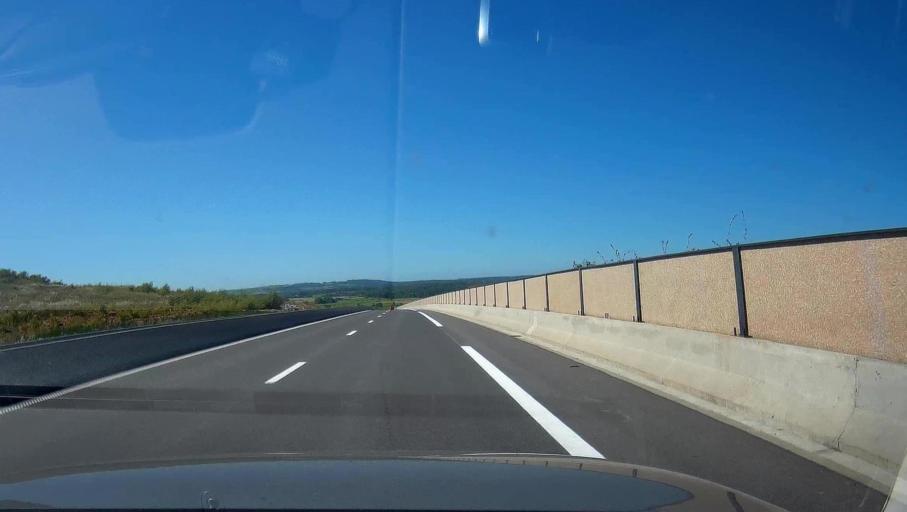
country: FR
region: Champagne-Ardenne
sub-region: Departement des Ardennes
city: Tournes
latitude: 49.7821
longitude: 4.6078
